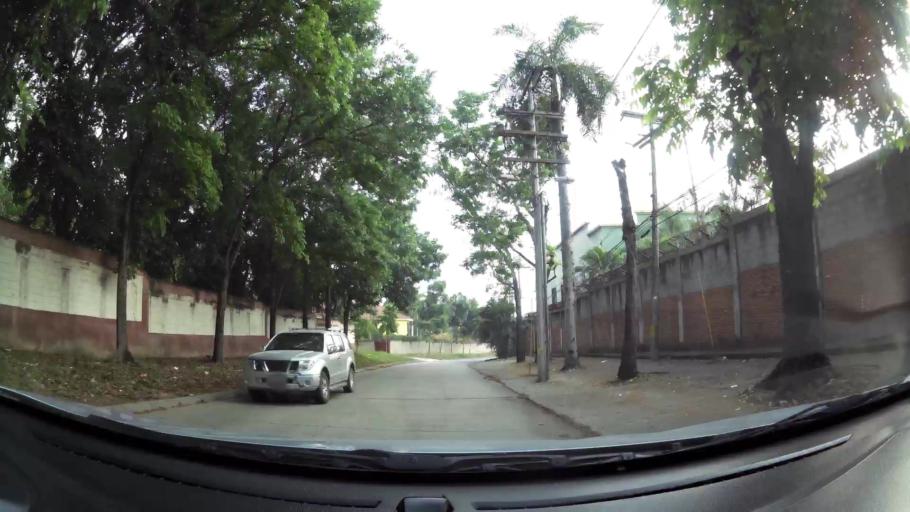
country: HN
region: Cortes
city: Armenta
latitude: 15.5065
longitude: -88.0471
